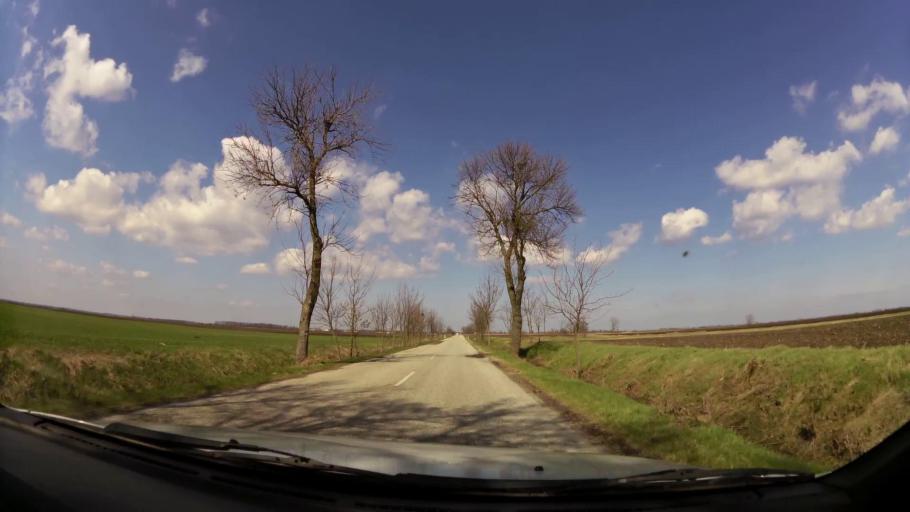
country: HU
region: Pest
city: Tapiogyorgye
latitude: 47.3095
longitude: 19.9428
